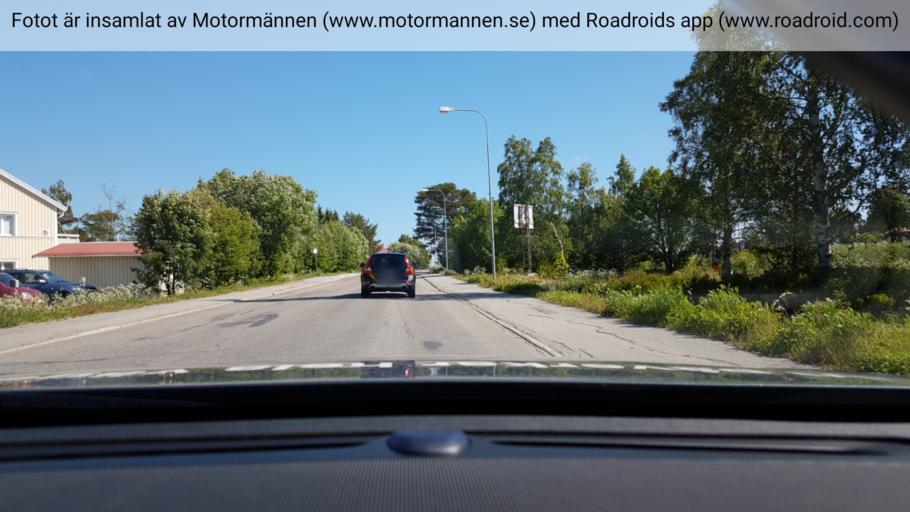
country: SE
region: Vaesterbotten
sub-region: Umea Kommun
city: Holmsund
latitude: 63.7121
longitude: 20.3752
